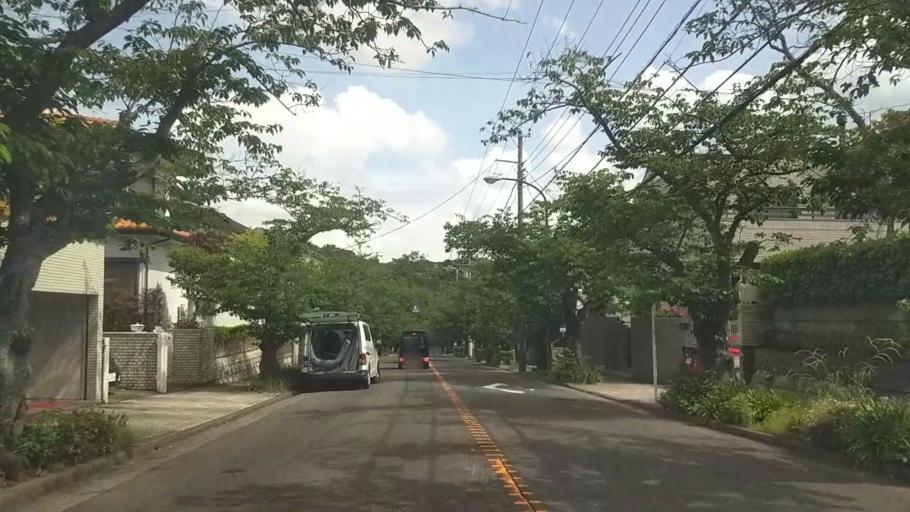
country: JP
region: Kanagawa
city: Zushi
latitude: 35.3154
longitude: 139.5767
